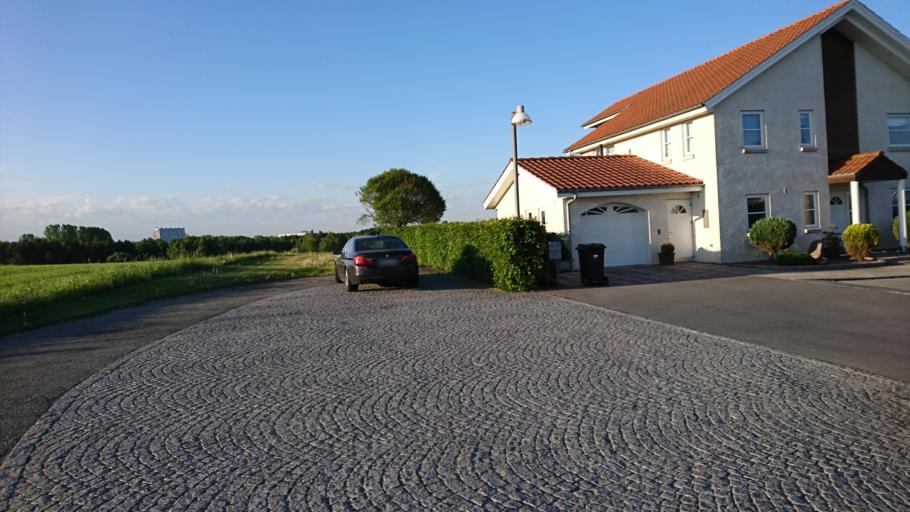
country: DK
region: Capital Region
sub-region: Ballerup Kommune
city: Malov
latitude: 55.7464
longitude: 12.3377
